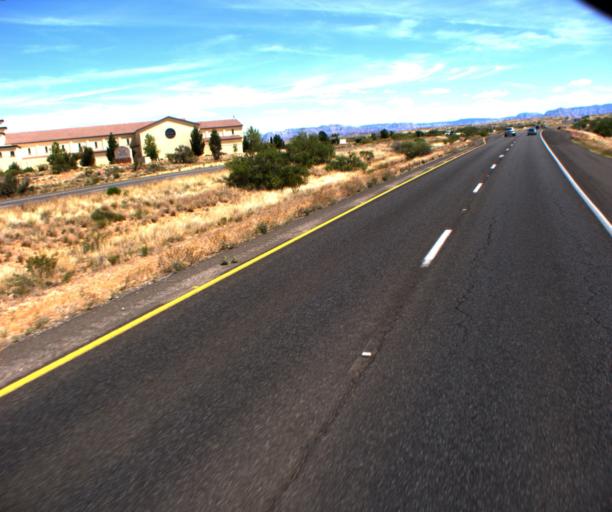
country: US
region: Arizona
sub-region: Yavapai County
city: Cottonwood
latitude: 34.7427
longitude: -111.9698
